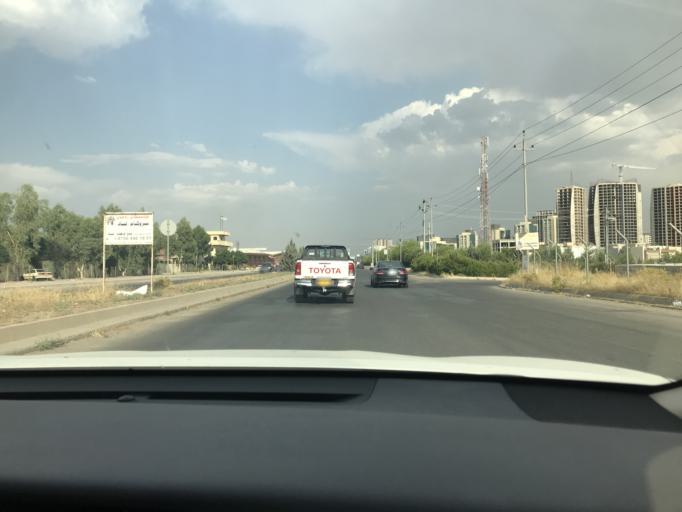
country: IQ
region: Arbil
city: Erbil
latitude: 36.2064
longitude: 43.9612
